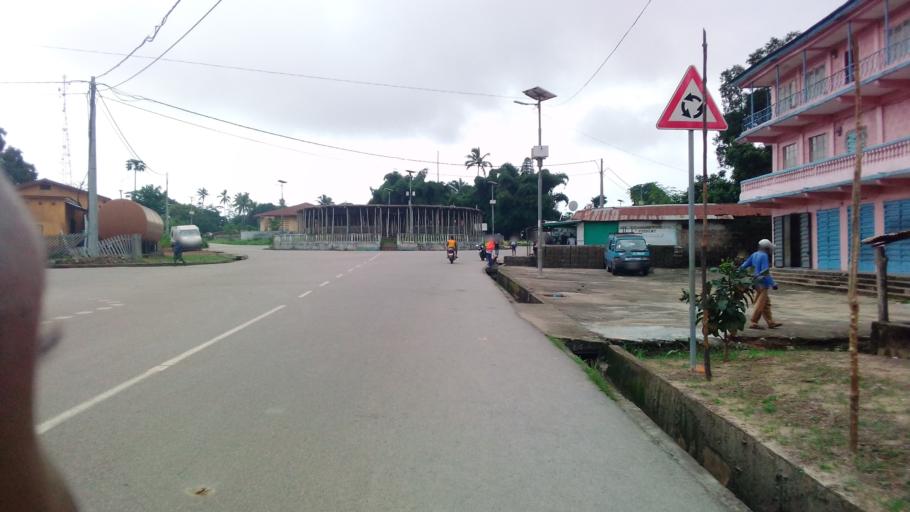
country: SL
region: Northern Province
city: Lunsar
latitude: 8.6860
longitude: -12.5350
